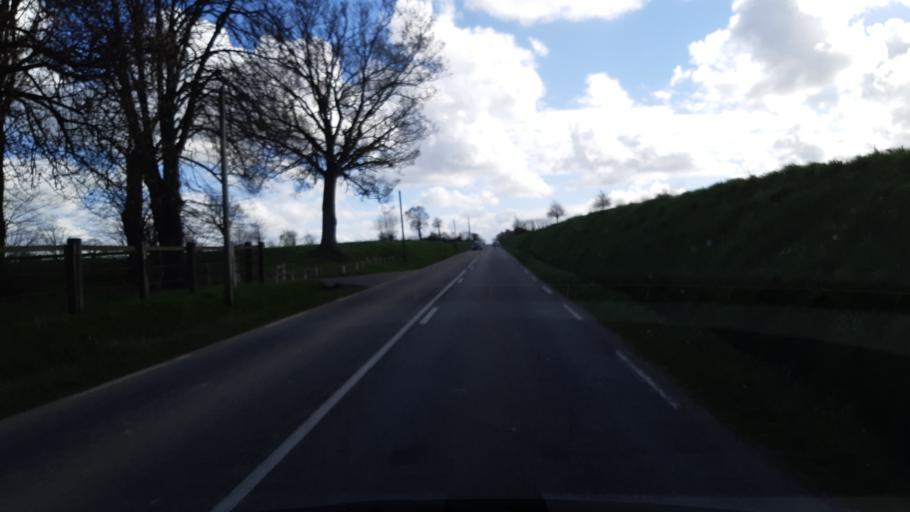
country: FR
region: Lower Normandy
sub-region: Departement de la Manche
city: Agneaux
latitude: 49.0644
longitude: -1.1326
